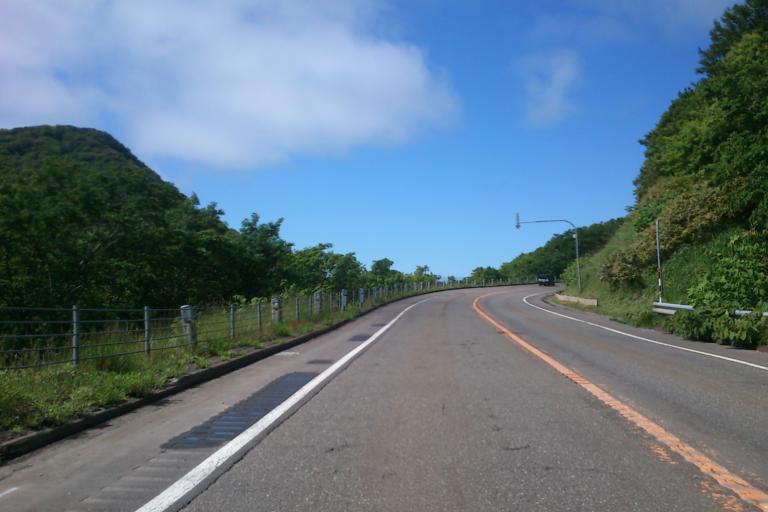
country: JP
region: Hokkaido
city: Ishikari
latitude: 43.4828
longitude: 141.3976
